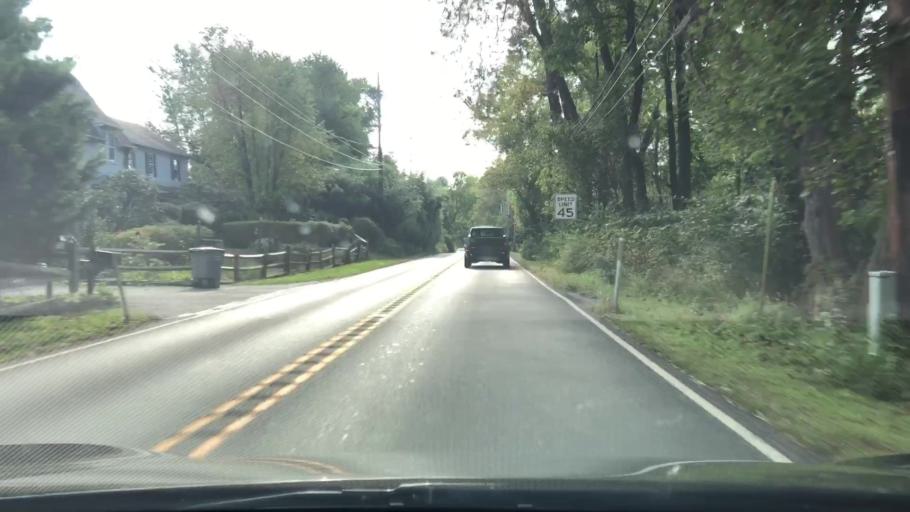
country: US
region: Pennsylvania
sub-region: Chester County
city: West Chester
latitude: 39.9283
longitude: -75.5582
